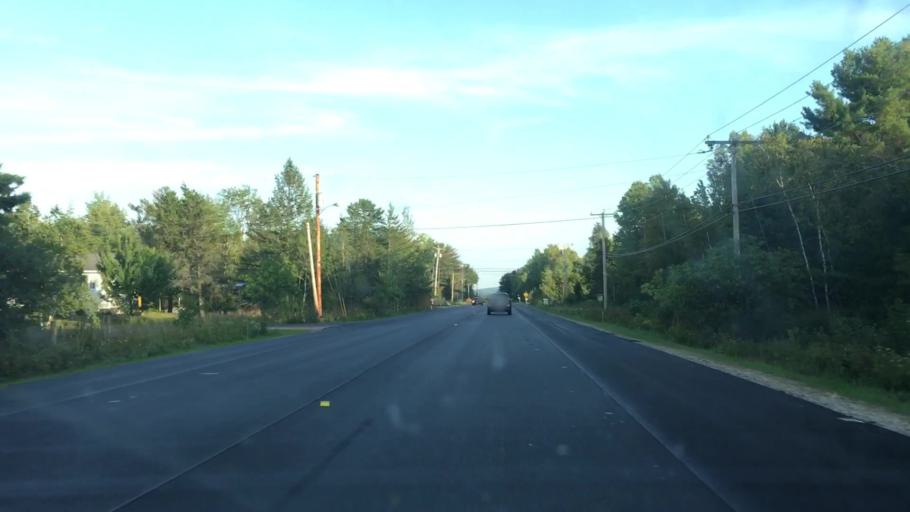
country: US
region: Maine
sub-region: Penobscot County
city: Hampden
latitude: 44.7590
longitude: -68.8456
